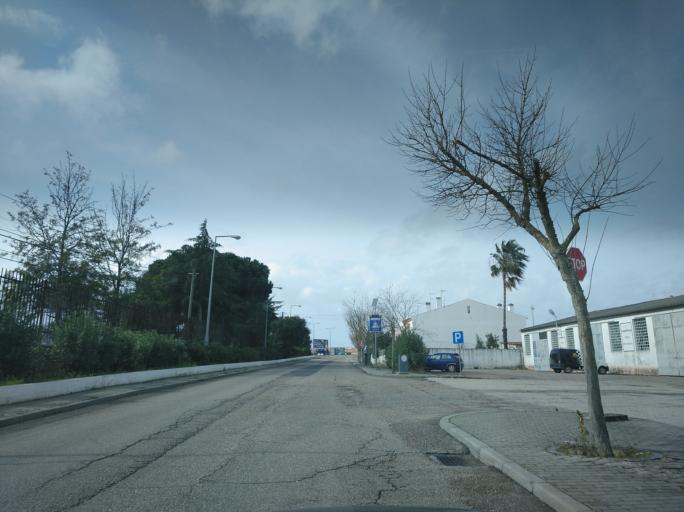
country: PT
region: Setubal
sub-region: Grandola
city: Grandola
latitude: 38.1708
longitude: -8.5570
